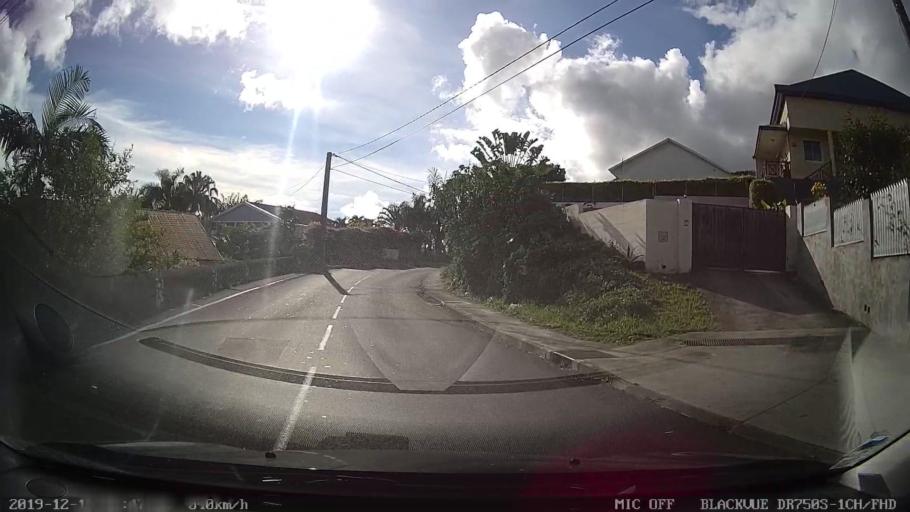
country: RE
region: Reunion
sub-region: Reunion
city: Le Tampon
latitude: -21.2452
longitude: 55.5143
